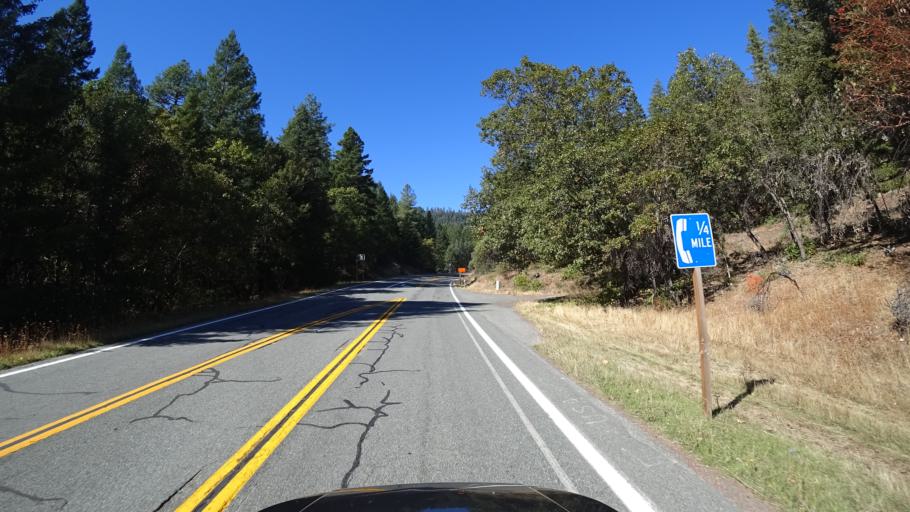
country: US
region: California
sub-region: Siskiyou County
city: Happy Camp
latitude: 41.3817
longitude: -123.4914
